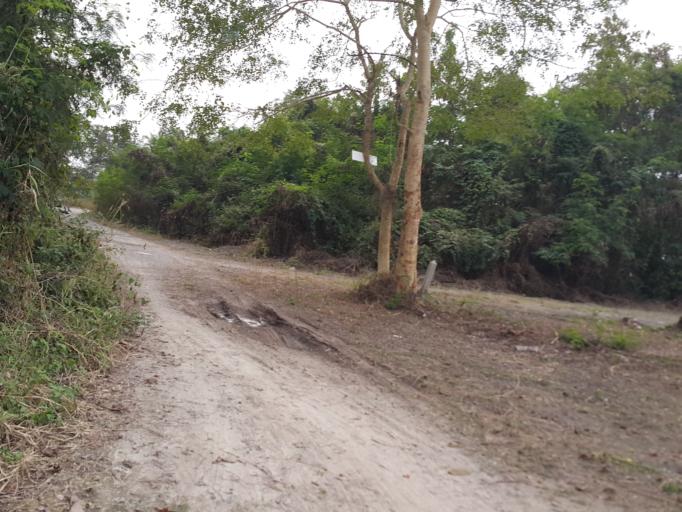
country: TH
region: Chiang Mai
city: San Kamphaeng
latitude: 18.8016
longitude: 99.1189
